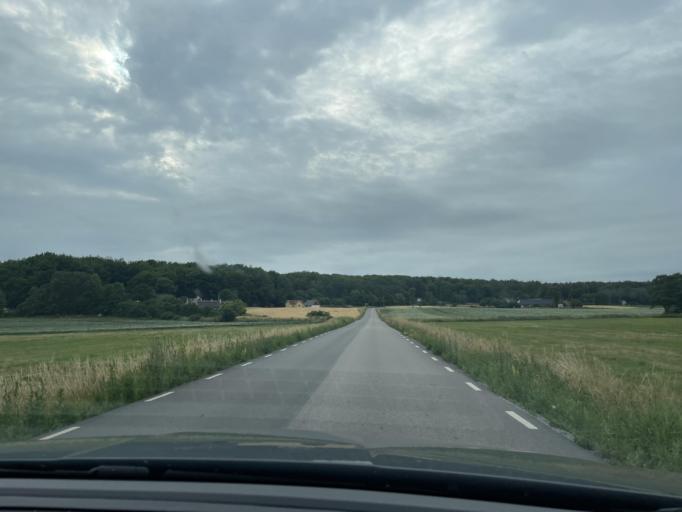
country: SE
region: Blekinge
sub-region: Solvesborgs Kommun
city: Soelvesborg
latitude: 56.0244
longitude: 14.6427
